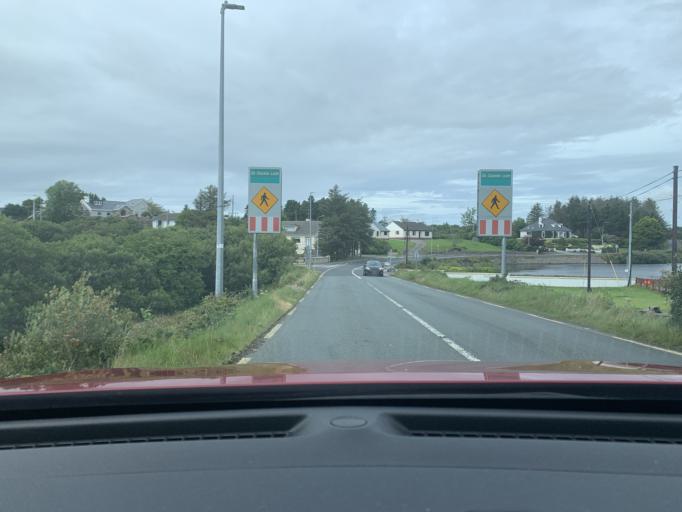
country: IE
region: Ulster
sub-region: County Donegal
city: Dungloe
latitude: 54.9477
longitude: -8.3410
